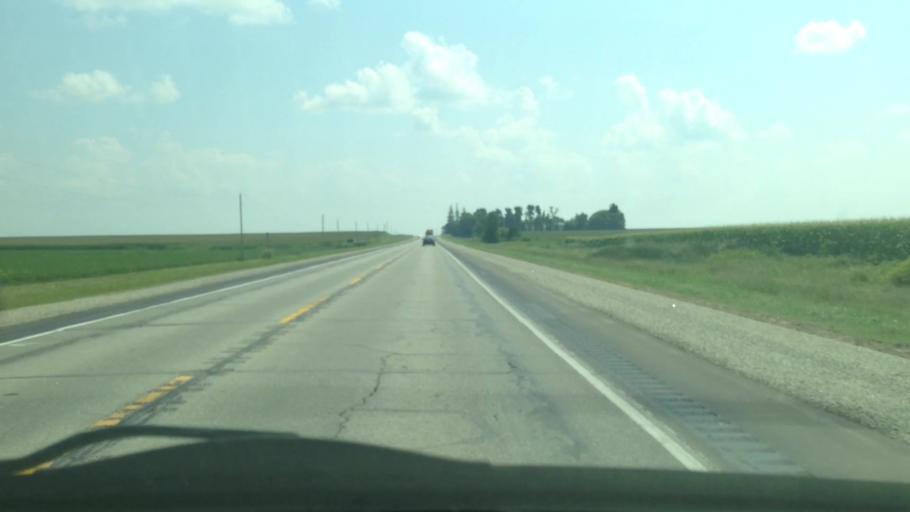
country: US
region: Iowa
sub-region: Howard County
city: Cresco
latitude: 43.4124
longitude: -92.2987
